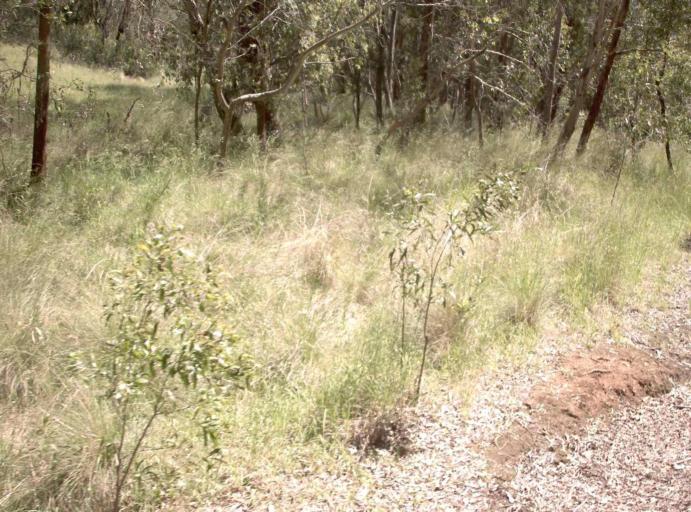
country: AU
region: Victoria
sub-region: East Gippsland
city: Lakes Entrance
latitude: -37.2384
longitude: 148.2585
